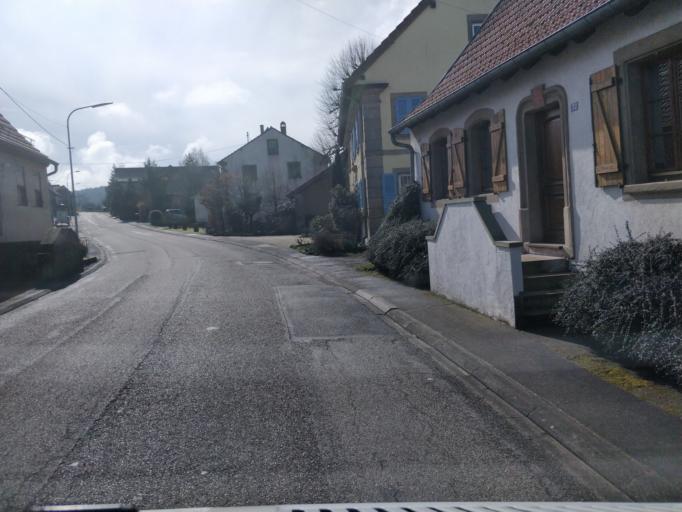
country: FR
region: Alsace
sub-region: Departement du Bas-Rhin
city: Drulingen
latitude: 48.8901
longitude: 7.2547
